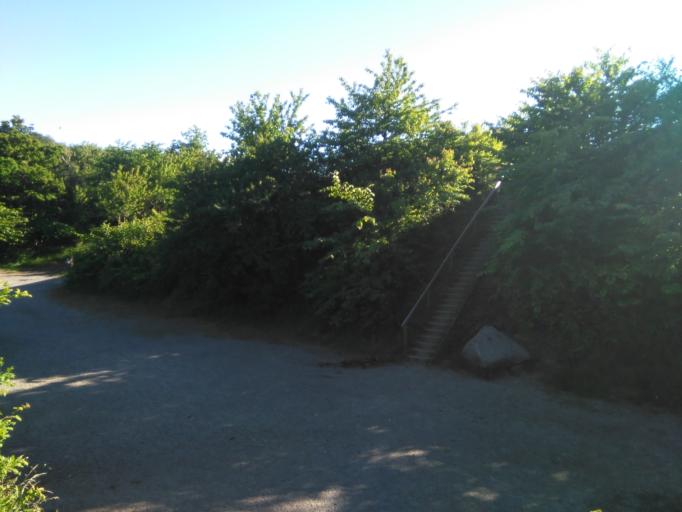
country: DK
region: Capital Region
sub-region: Bornholm Kommune
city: Ronne
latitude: 55.2819
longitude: 14.7614
